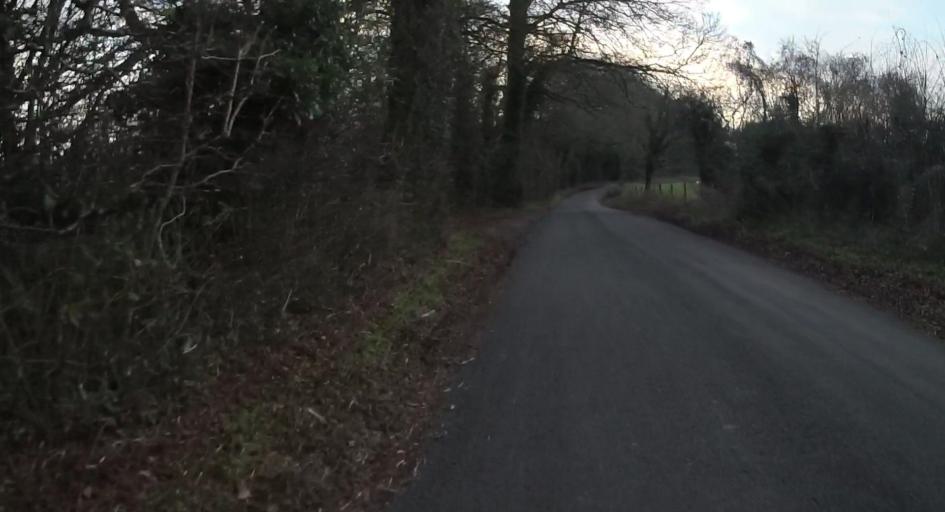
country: GB
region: England
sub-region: Hampshire
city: Swanmore
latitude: 51.0149
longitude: -1.1558
